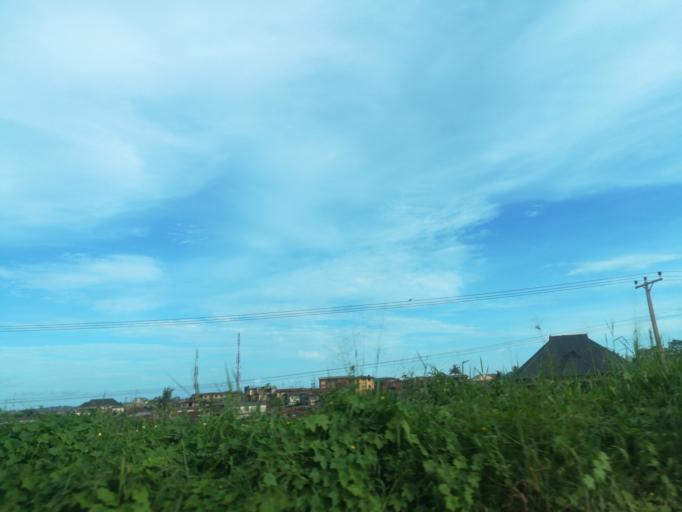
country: NG
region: Oyo
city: Ibadan
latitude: 7.3578
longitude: 3.9224
